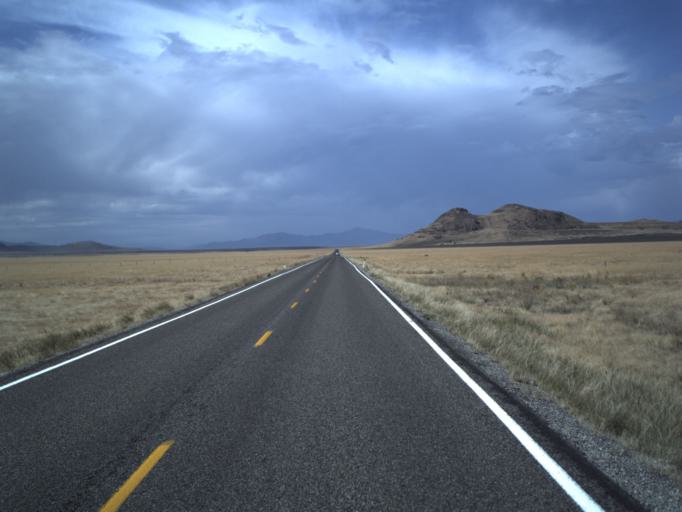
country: US
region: Utah
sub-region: Tooele County
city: Wendover
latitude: 41.3937
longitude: -113.9662
